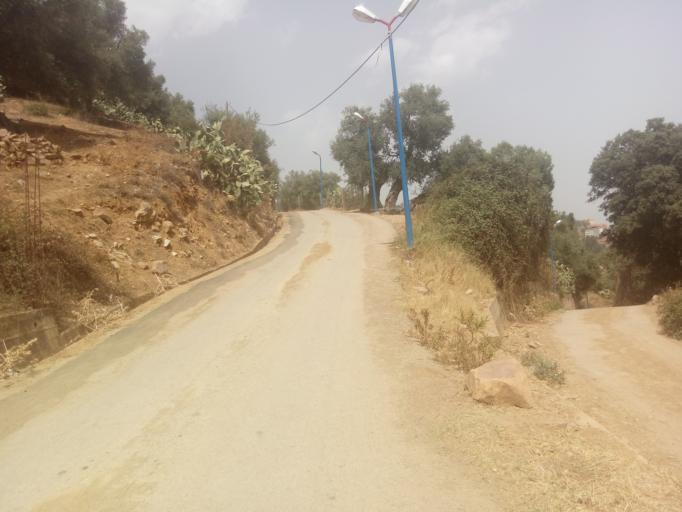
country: DZ
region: Tizi Ouzou
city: Chemini
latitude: 36.6029
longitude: 4.6378
